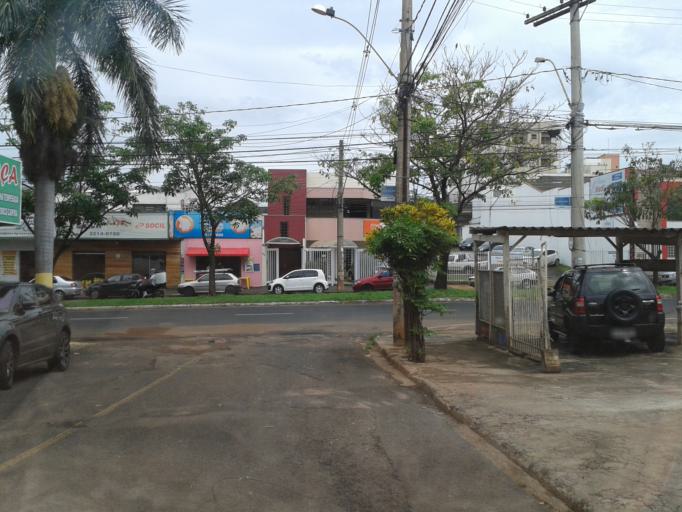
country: BR
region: Minas Gerais
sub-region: Uberlandia
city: Uberlandia
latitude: -18.9252
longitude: -48.2938
